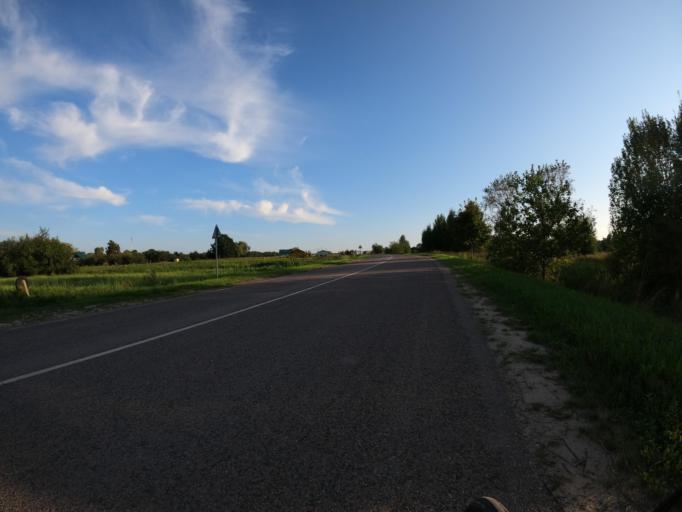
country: RU
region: Moskovskaya
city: Meshcherino
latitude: 55.1181
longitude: 38.3217
